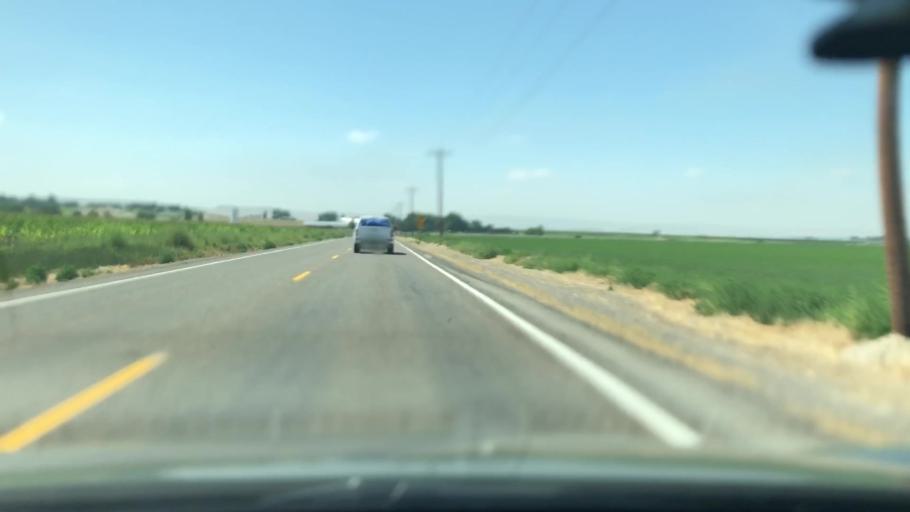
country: US
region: Idaho
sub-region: Owyhee County
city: Marsing
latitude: 43.5452
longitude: -116.8824
